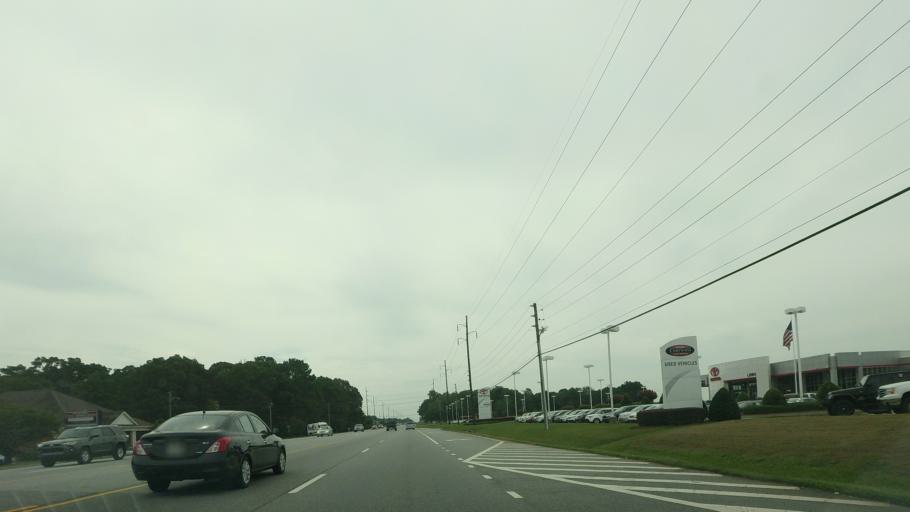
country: US
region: Georgia
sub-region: Houston County
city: Centerville
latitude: 32.6109
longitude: -83.6790
